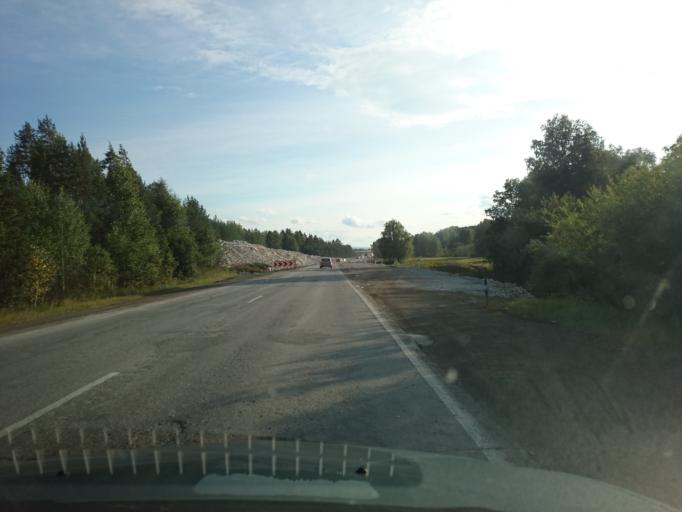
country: RU
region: Bashkortostan
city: Lomovka
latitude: 53.9110
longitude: 58.1783
